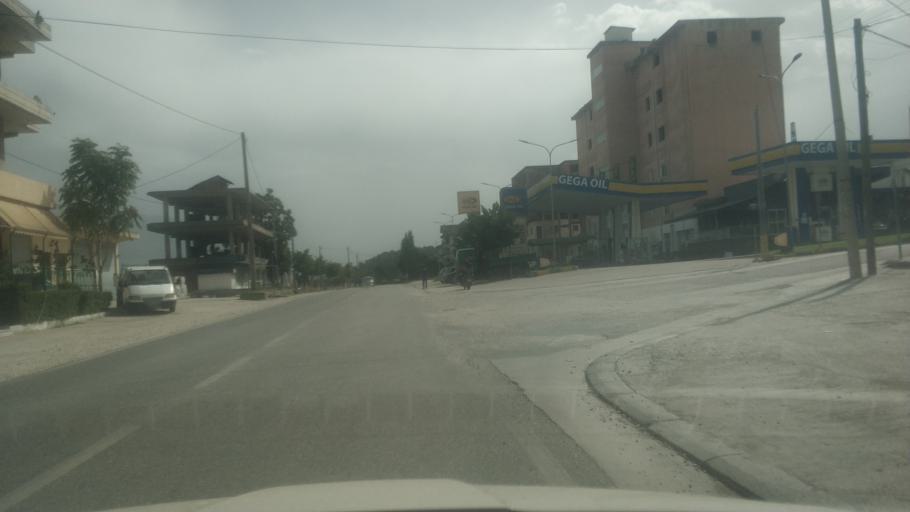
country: AL
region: Gjirokaster
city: Gjirokaster
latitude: 40.0744
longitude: 20.1547
